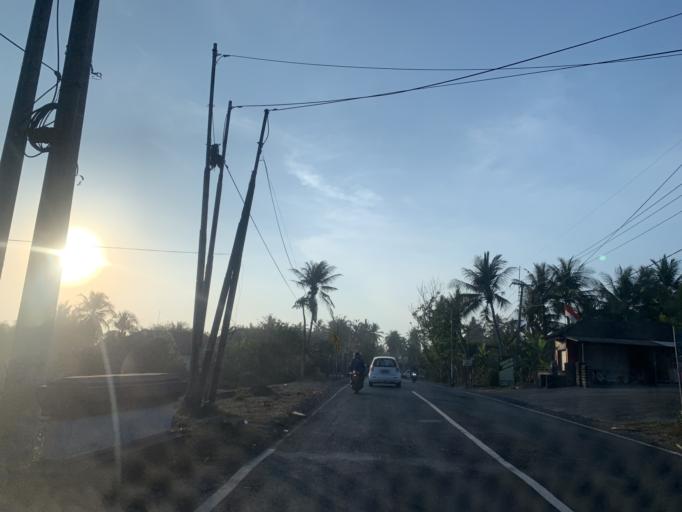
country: ID
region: Bali
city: Banjar Swastika
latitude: -8.4591
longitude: 114.9043
